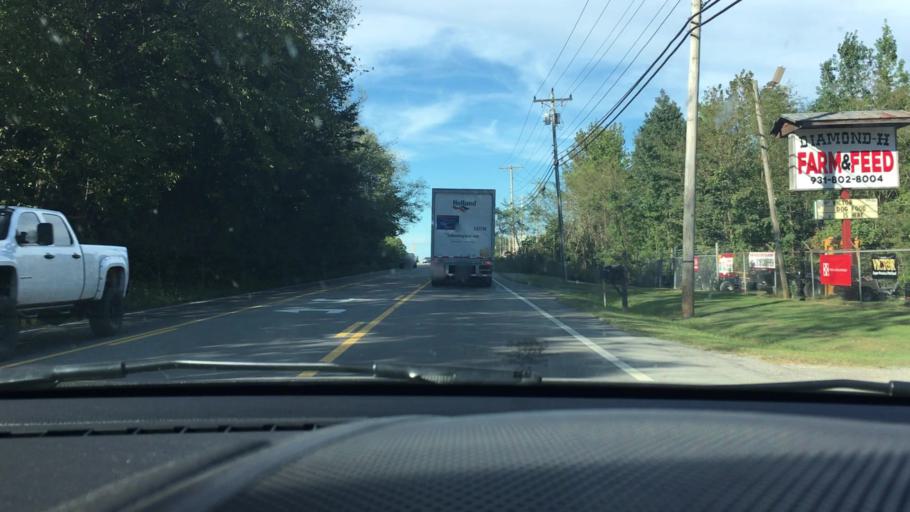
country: US
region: Tennessee
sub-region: Montgomery County
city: Clarksville
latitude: 36.4759
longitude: -87.3764
